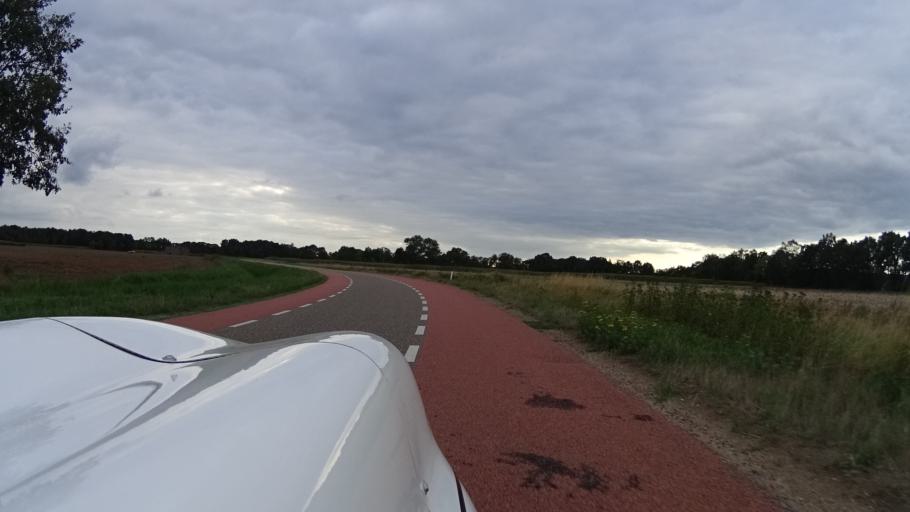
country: NL
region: North Brabant
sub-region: Gemeente Bernheze
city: Loosbroek
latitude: 51.6910
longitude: 5.4775
